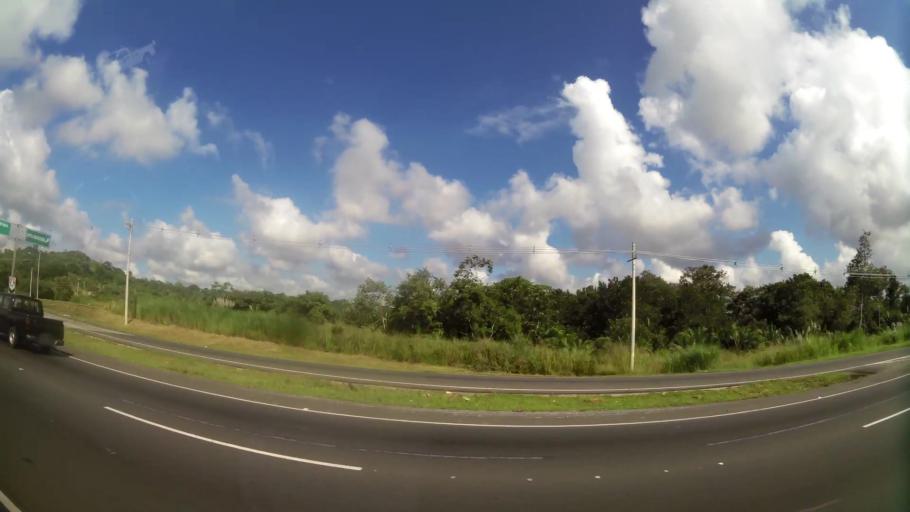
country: PA
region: Panama
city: Nuevo Arraijan
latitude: 8.9110
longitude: -79.7273
